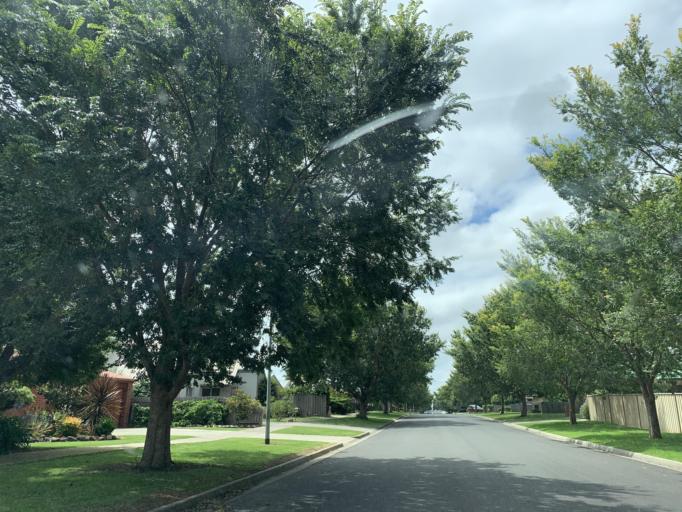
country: AU
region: Victoria
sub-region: Wellington
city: Sale
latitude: -38.1193
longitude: 147.0870
